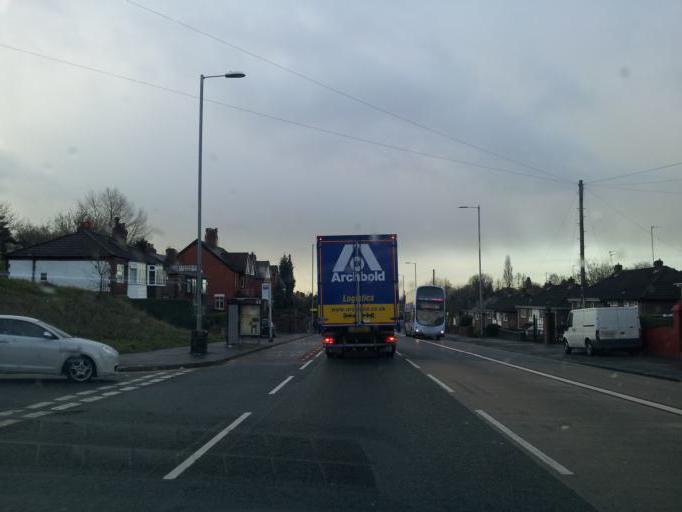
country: GB
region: England
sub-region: Manchester
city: Blackley
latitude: 53.5293
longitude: -2.2107
